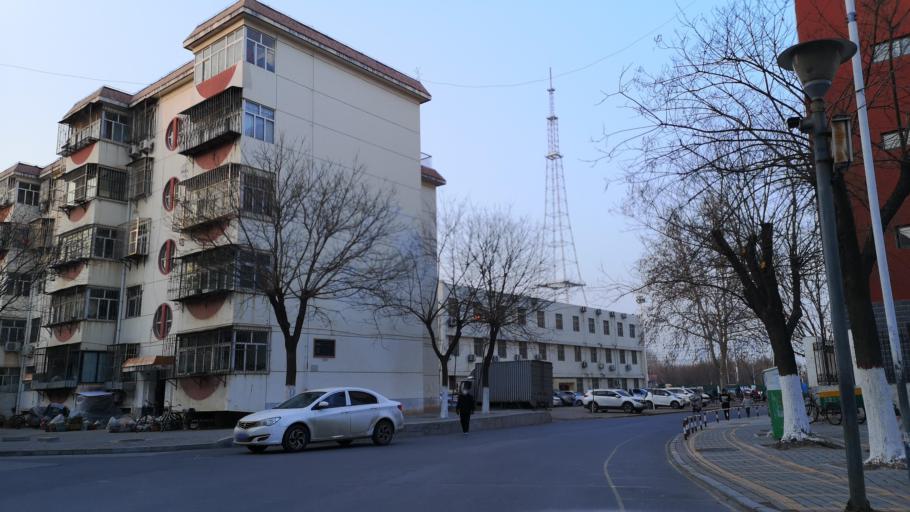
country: CN
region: Henan Sheng
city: Zhongyuanlu
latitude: 35.7700
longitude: 115.0791
